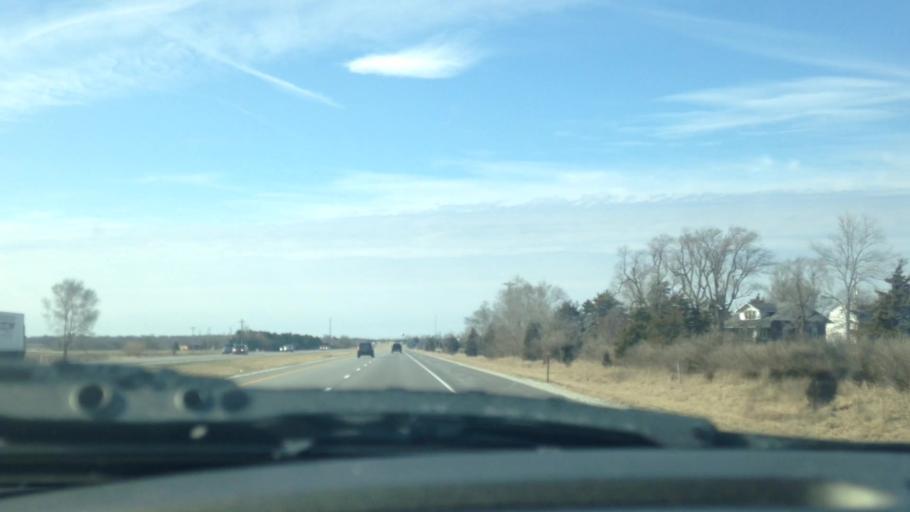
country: US
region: Illinois
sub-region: Ford County
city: Paxton
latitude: 40.4860
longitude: -88.0976
